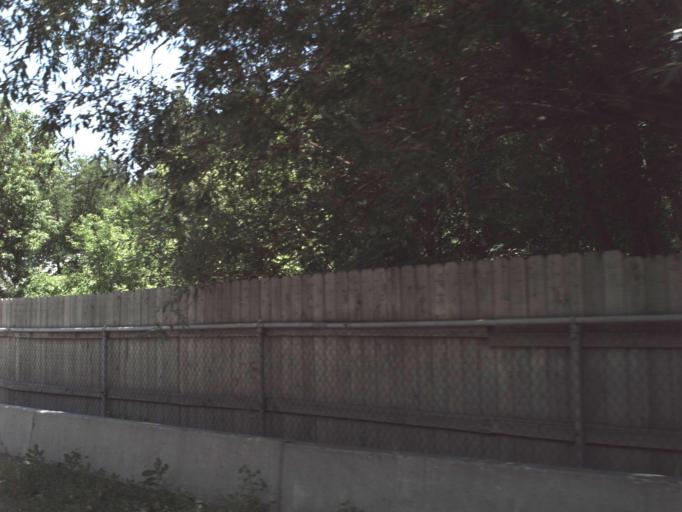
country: US
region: Utah
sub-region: Weber County
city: Liberty
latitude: 41.2542
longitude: -111.8737
